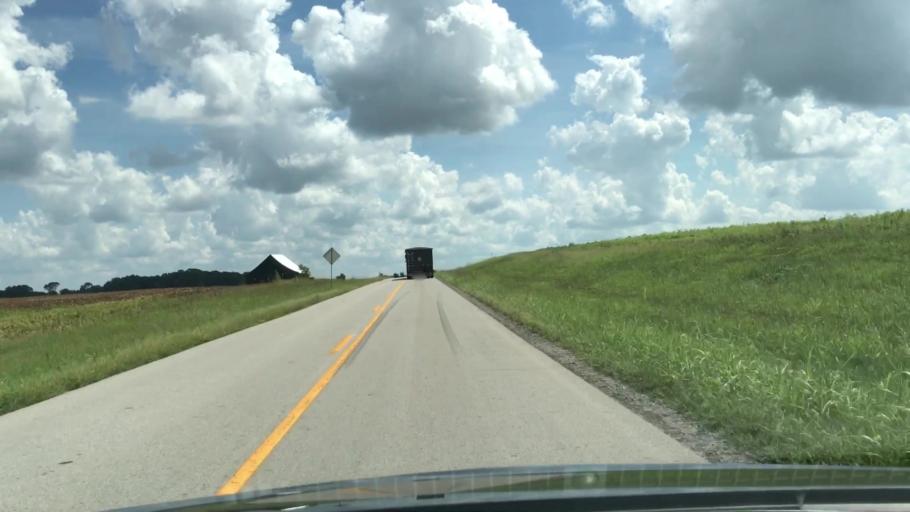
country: US
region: Kentucky
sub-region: Todd County
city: Guthrie
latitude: 36.6508
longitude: -87.0039
